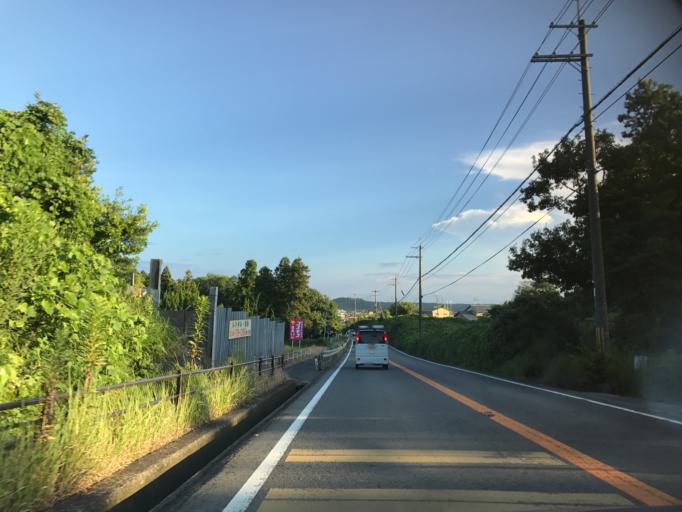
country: JP
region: Shiga Prefecture
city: Hino
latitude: 35.0268
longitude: 136.2393
